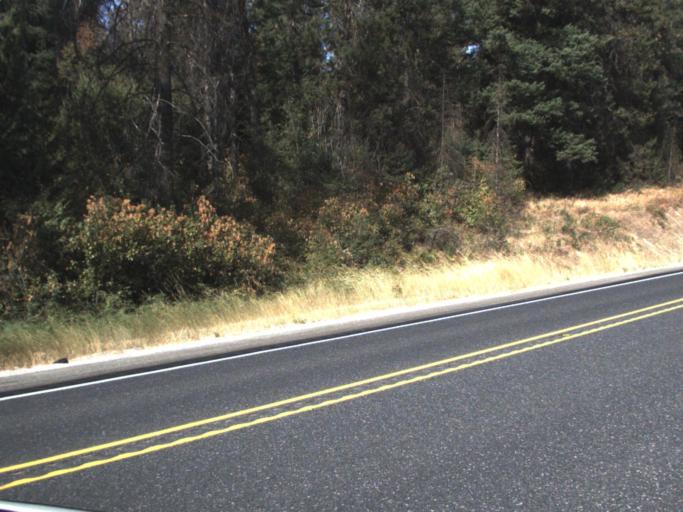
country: US
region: Washington
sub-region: Spokane County
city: Deer Park
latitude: 48.0229
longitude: -117.5926
